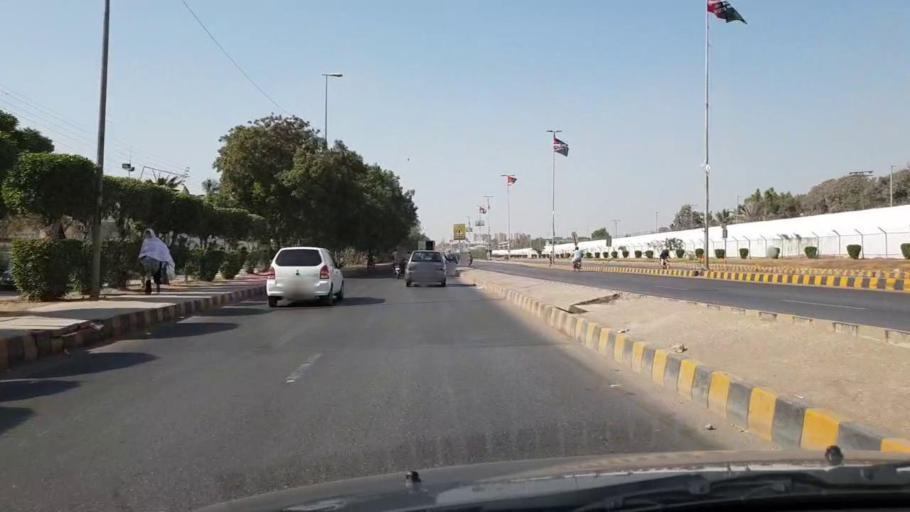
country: PK
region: Sindh
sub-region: Karachi District
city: Karachi
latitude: 24.8765
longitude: 67.0952
